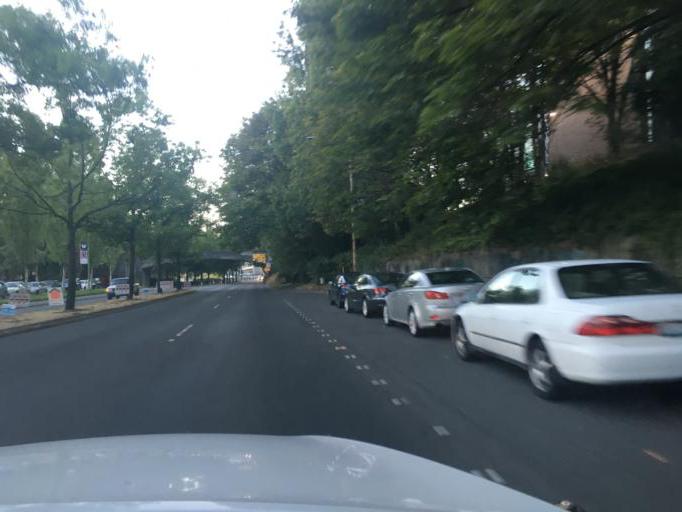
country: US
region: Washington
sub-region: King County
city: Seattle
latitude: 47.6539
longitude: -122.3028
